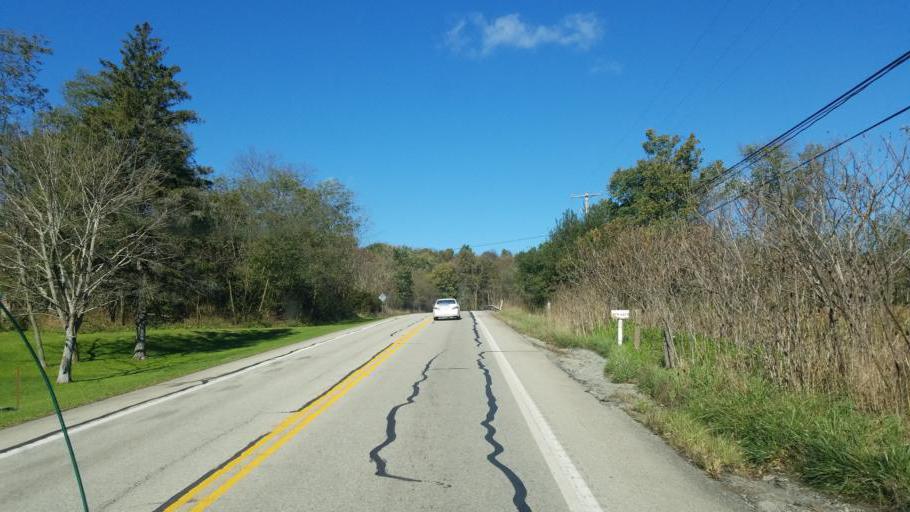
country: US
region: Pennsylvania
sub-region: Somerset County
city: Friedens
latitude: 40.1133
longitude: -78.9719
